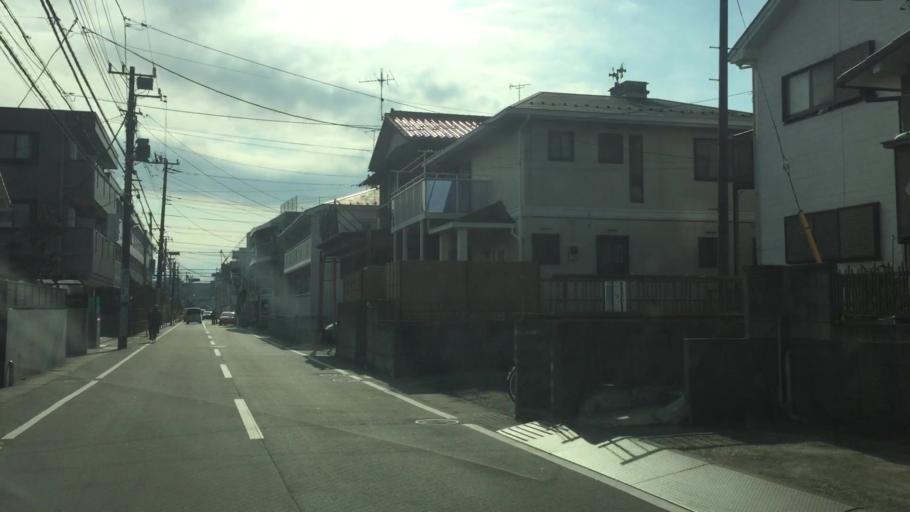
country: JP
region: Tokyo
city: Urayasu
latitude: 35.6760
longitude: 139.8998
